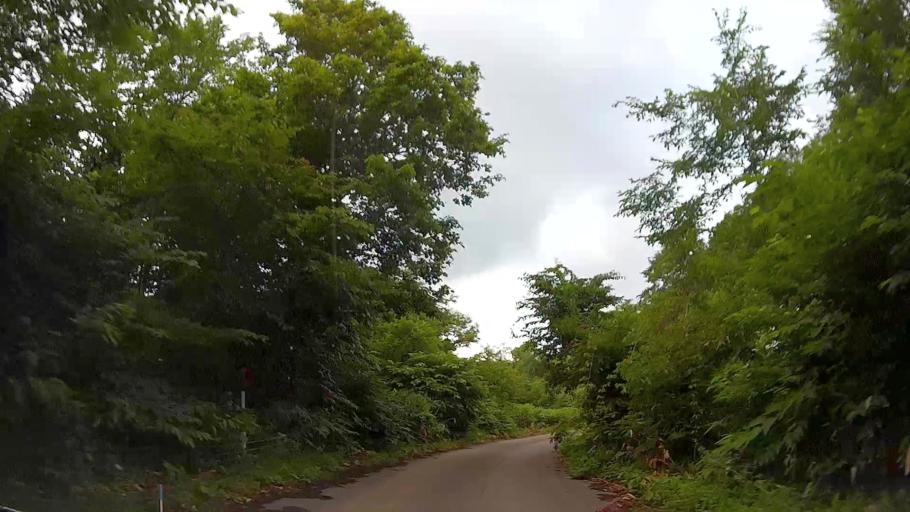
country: JP
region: Hokkaido
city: Nanae
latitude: 42.1049
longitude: 140.4514
